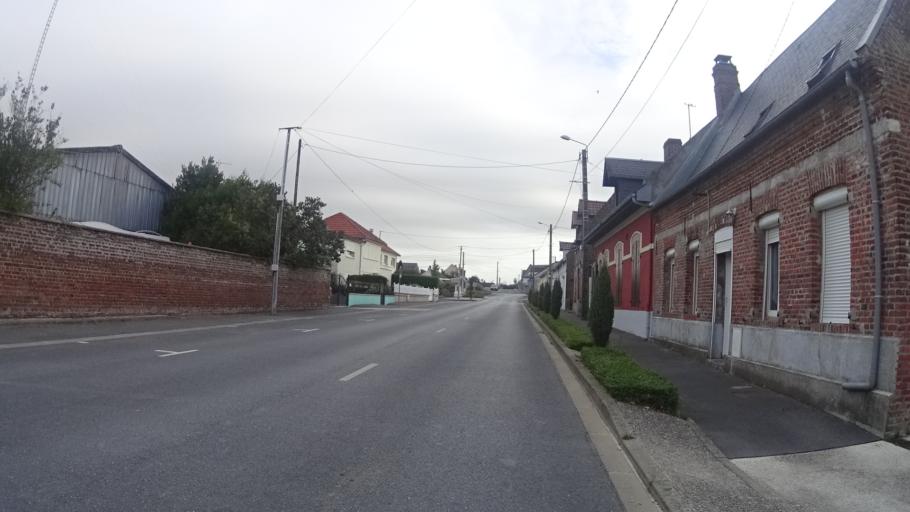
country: FR
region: Picardie
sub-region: Departement de l'Aisne
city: Origny-Sainte-Benoite
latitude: 49.8323
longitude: 3.4699
